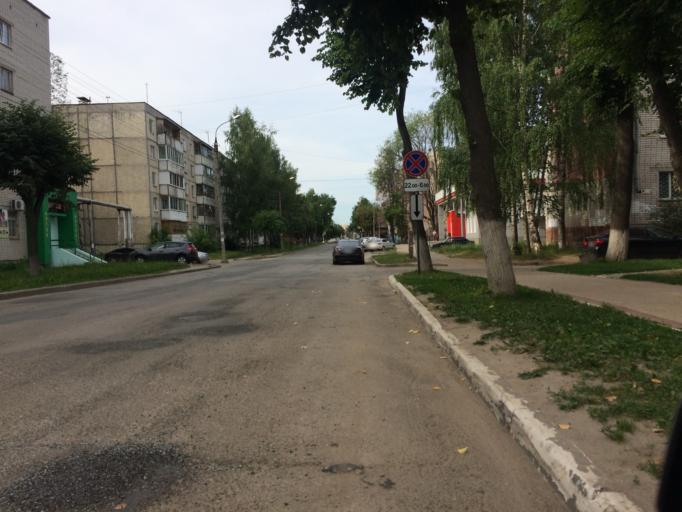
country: RU
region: Mariy-El
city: Yoshkar-Ola
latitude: 56.6431
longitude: 47.9031
